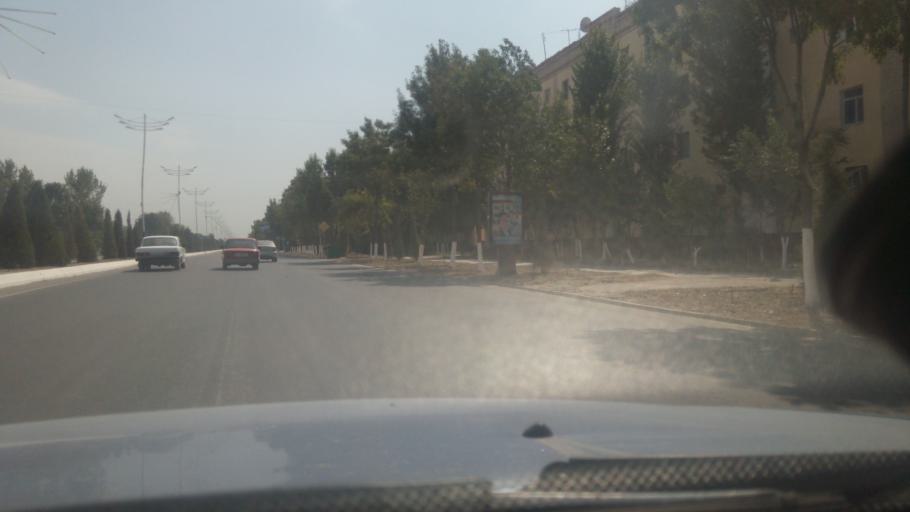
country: UZ
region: Sirdaryo
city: Guliston
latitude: 40.5022
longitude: 68.7733
